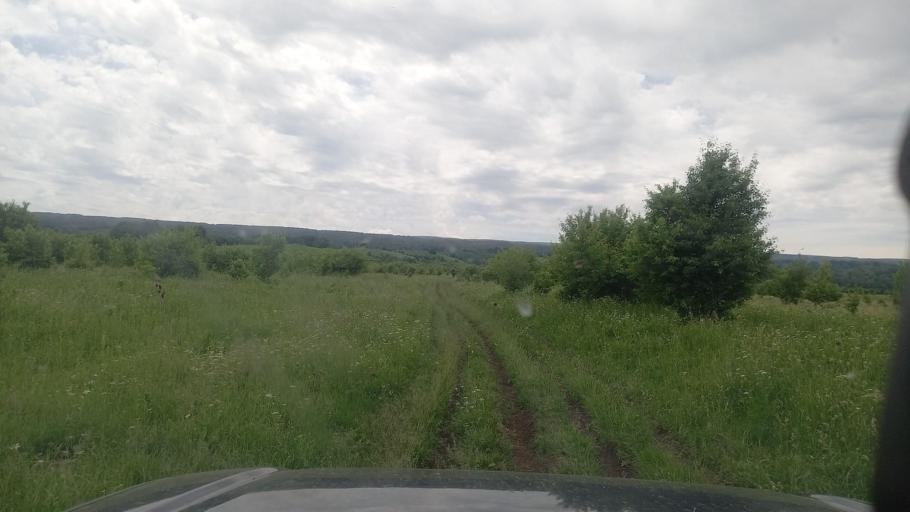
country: RU
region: Karachayevo-Cherkesiya
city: Pregradnaya
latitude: 44.0996
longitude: 41.1926
